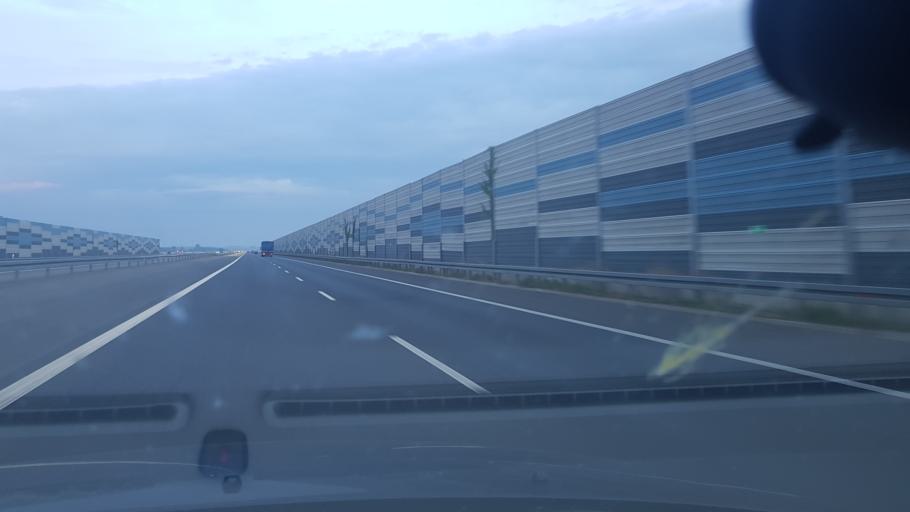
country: PL
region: Lodz Voivodeship
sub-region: Powiat zgierski
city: Strykow
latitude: 51.9767
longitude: 19.5669
